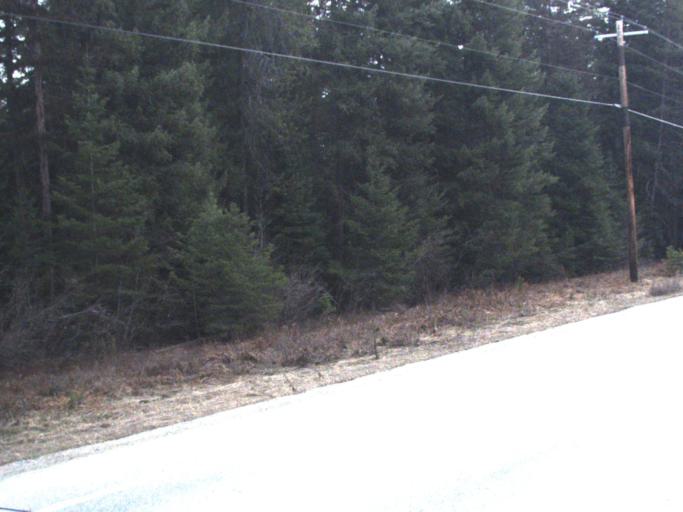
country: US
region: Washington
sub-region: Pend Oreille County
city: Newport
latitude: 48.2690
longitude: -117.2596
